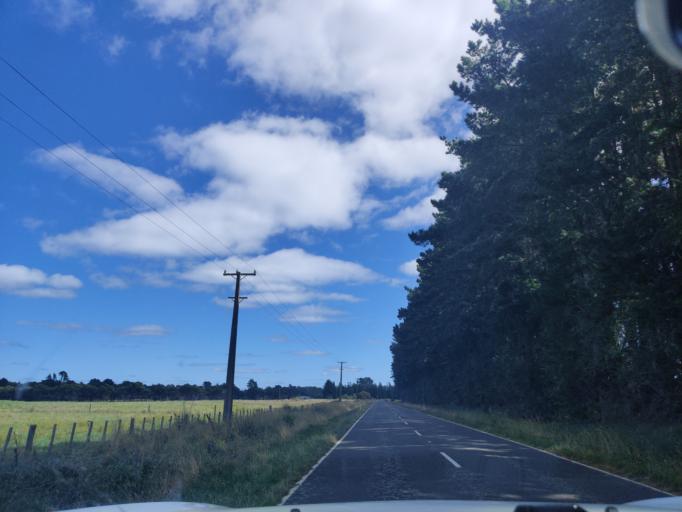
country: NZ
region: Manawatu-Wanganui
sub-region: Horowhenua District
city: Foxton
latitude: -40.3814
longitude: 175.2626
